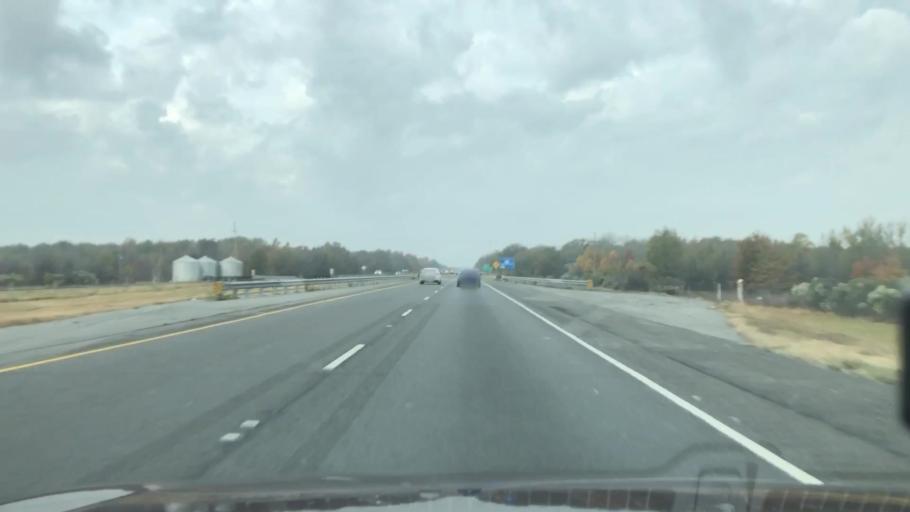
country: US
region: Louisiana
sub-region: Richland Parish
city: Delhi
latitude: 32.4387
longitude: -91.4668
